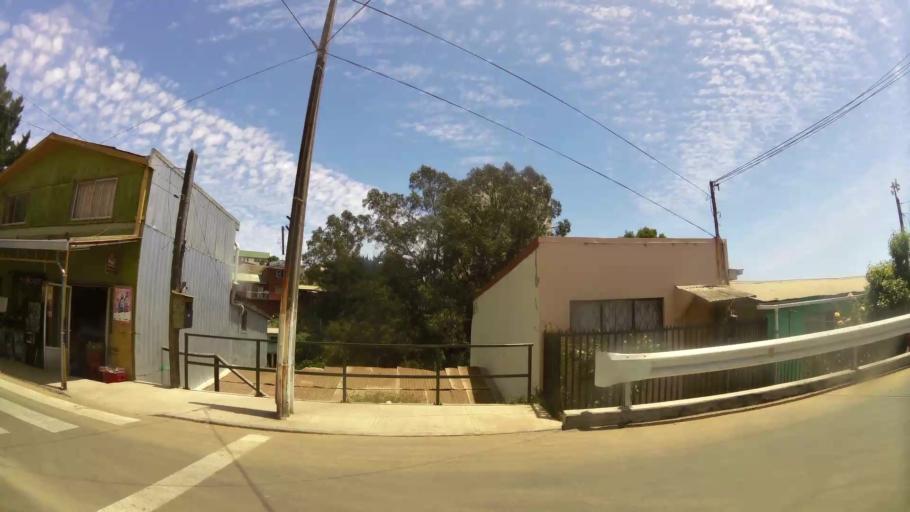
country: CL
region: Valparaiso
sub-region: Provincia de Valparaiso
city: Vina del Mar
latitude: -33.0432
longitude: -71.5868
